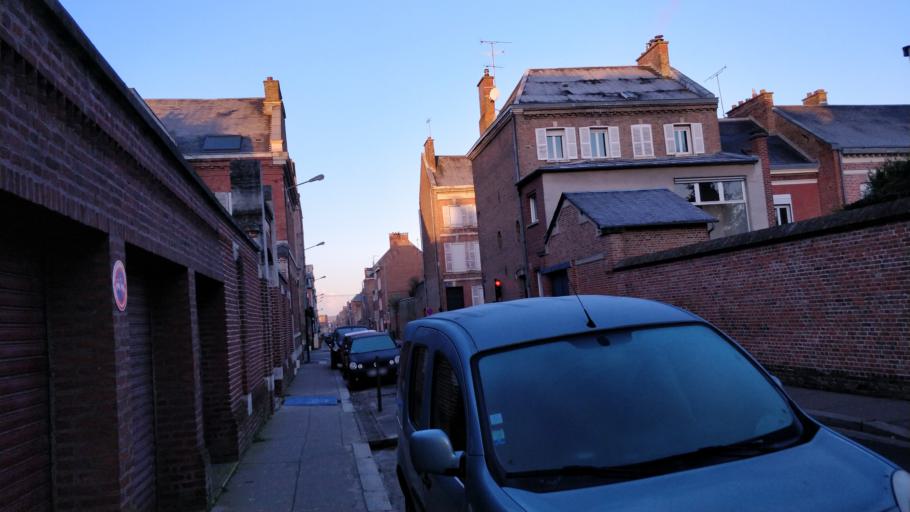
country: FR
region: Picardie
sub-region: Departement de la Somme
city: Amiens
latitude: 49.8856
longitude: 2.2964
